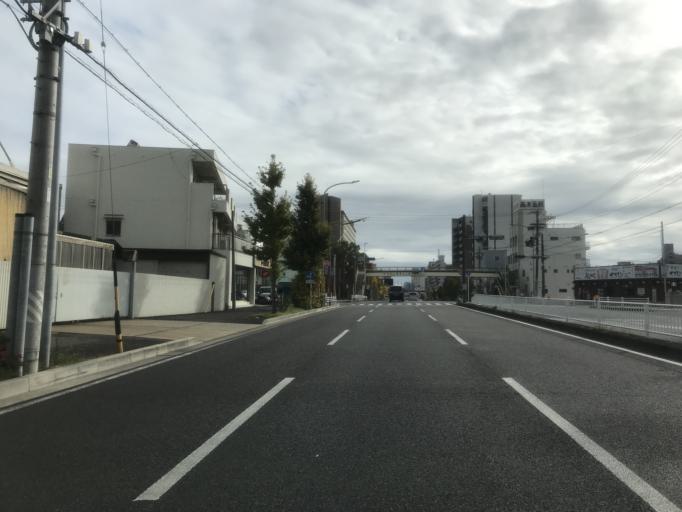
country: JP
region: Aichi
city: Nagoya-shi
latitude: 35.1889
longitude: 136.8721
